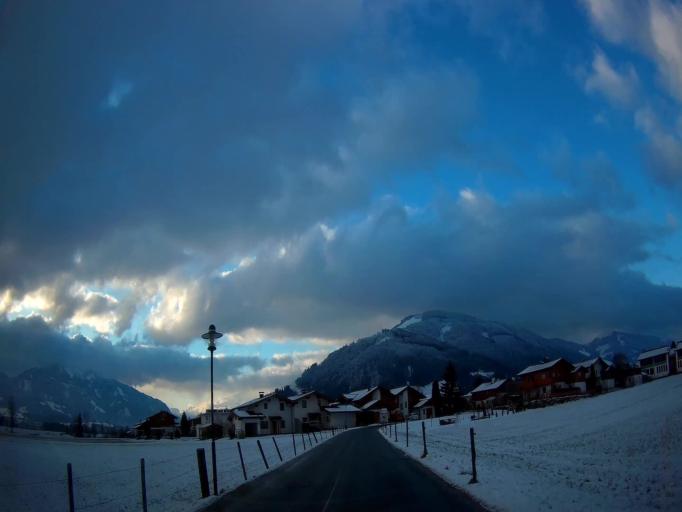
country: AT
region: Salzburg
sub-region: Politischer Bezirk Zell am See
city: Saalfelden am Steinernen Meer
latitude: 47.4481
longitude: 12.8187
